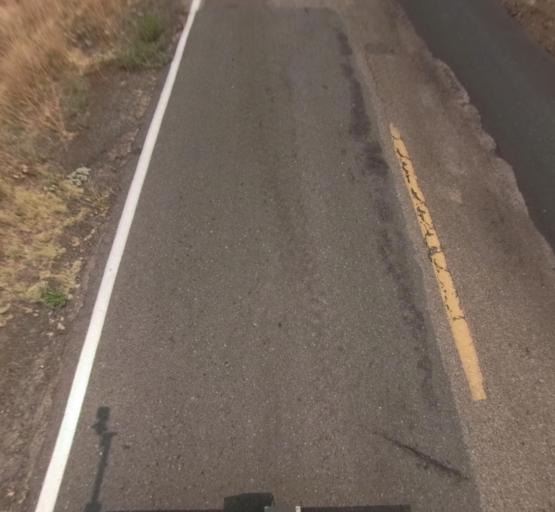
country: US
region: California
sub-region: Madera County
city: Bonadelle Ranchos-Madera Ranchos
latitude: 37.1118
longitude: -119.9388
